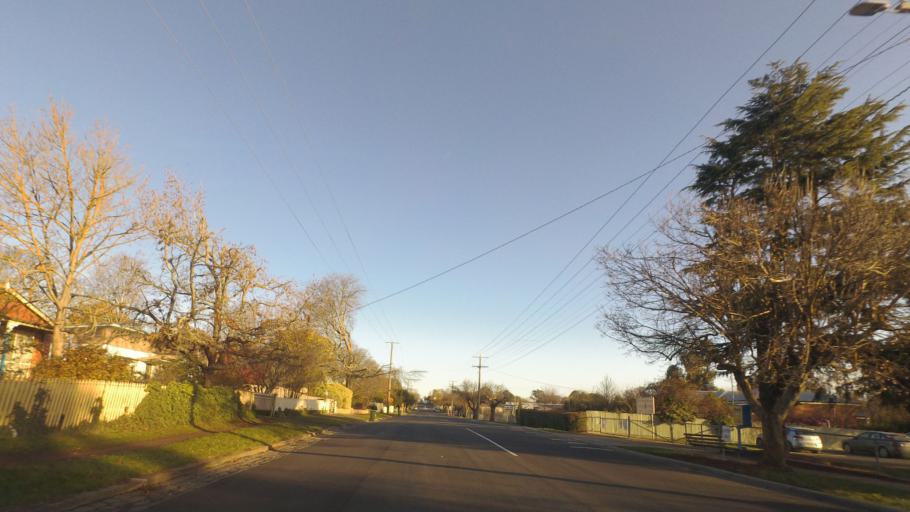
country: AU
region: Victoria
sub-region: Mount Alexander
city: Castlemaine
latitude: -37.2496
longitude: 144.4627
